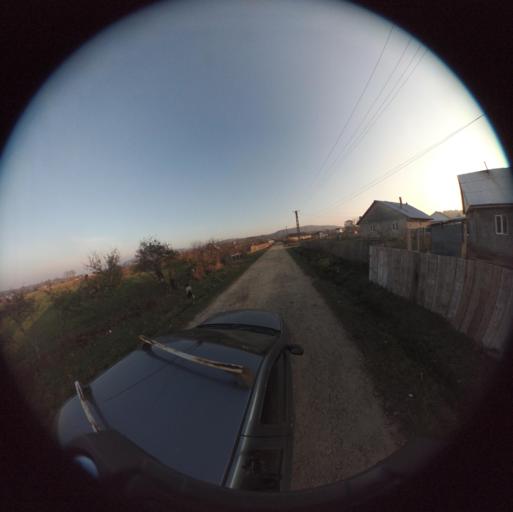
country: RO
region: Vaslui
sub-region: Comuna Bacesti
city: Bacesti
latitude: 46.8304
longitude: 27.2476
